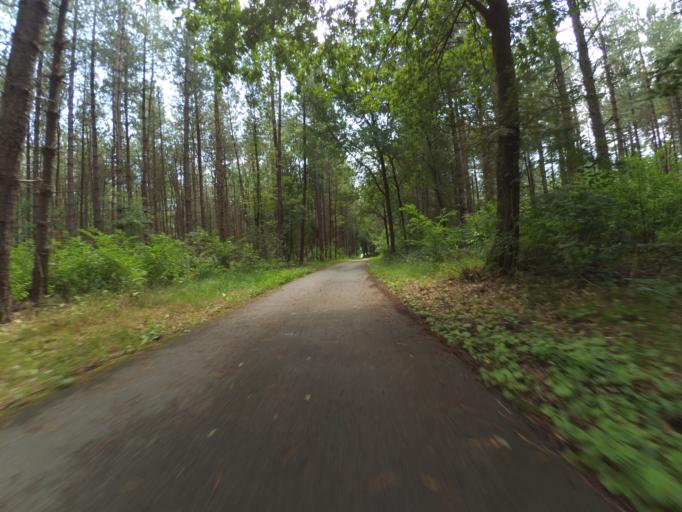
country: BE
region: Flanders
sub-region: Provincie Limburg
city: Opglabbeek
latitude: 51.0777
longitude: 5.6197
